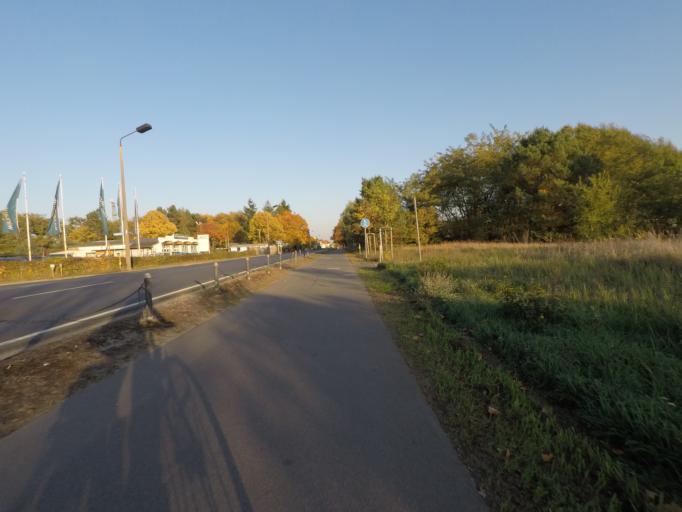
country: DE
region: Brandenburg
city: Melchow
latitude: 52.8395
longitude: 13.7205
